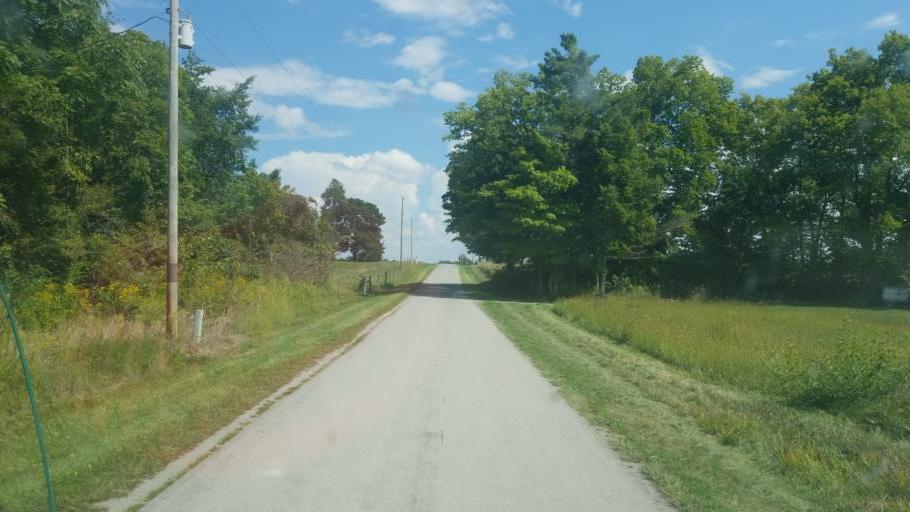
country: US
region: Ohio
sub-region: Wyandot County
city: Carey
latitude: 40.8757
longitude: -83.3863
